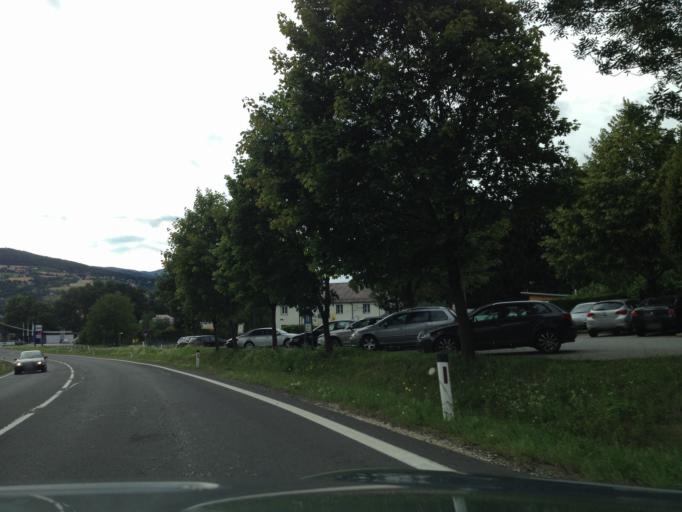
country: AT
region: Styria
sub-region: Politischer Bezirk Hartberg-Fuerstenfeld
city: Sankt Johann in der Haide
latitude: 47.2815
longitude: 16.0040
